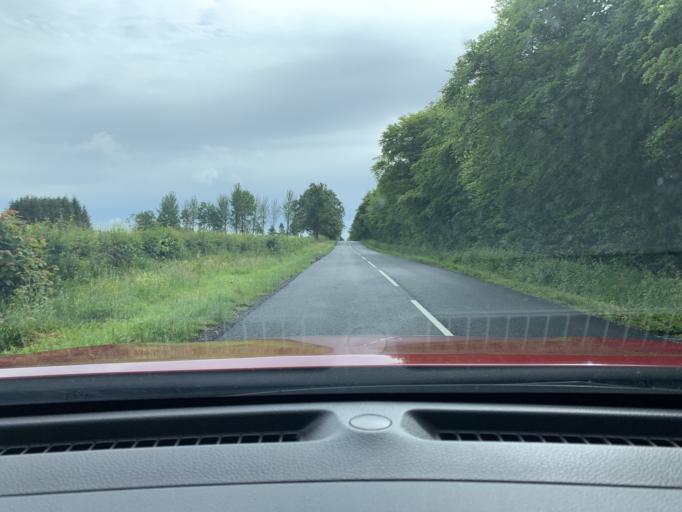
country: GB
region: Northern Ireland
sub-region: Fermanagh District
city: Enniskillen
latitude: 54.2595
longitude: -7.7494
